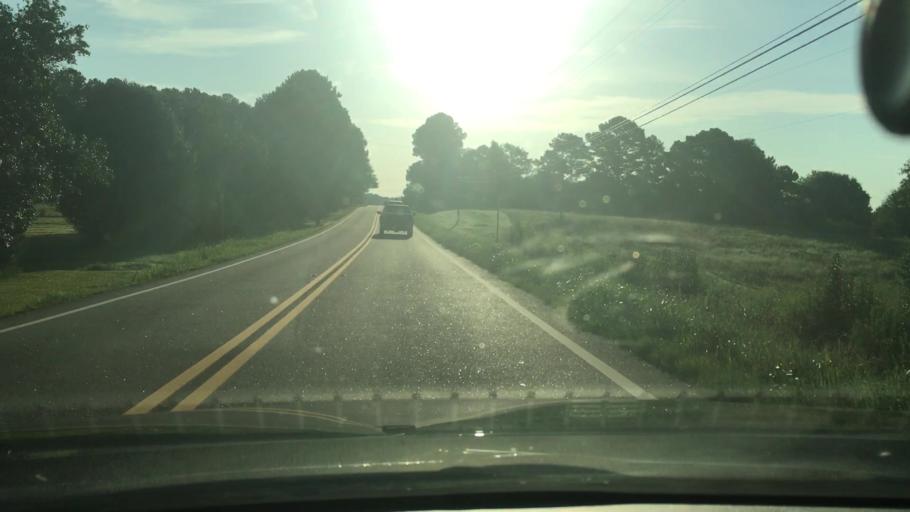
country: US
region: Georgia
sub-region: Fayette County
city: Peachtree City
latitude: 33.3854
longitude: -84.6552
